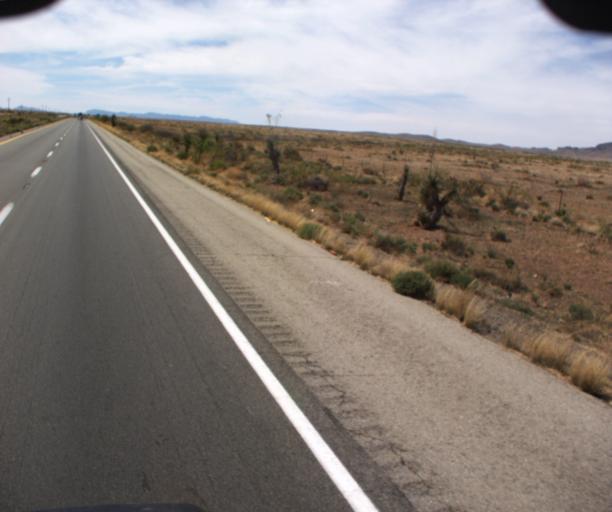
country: US
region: Arizona
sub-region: Cochise County
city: Willcox
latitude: 32.3624
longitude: -109.6510
